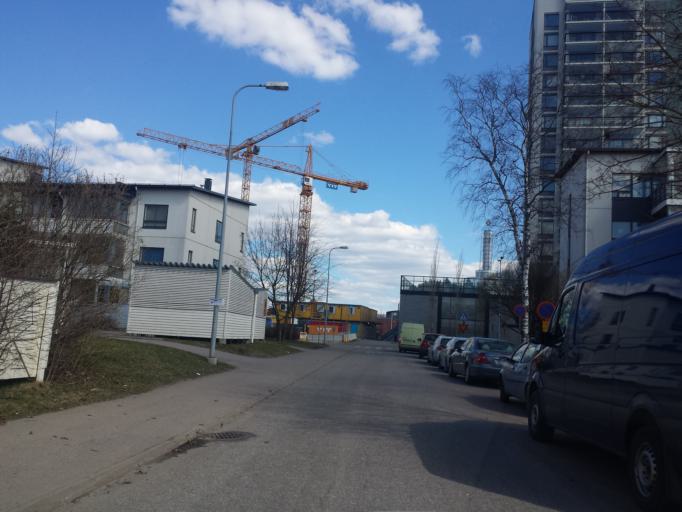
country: FI
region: Uusimaa
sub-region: Helsinki
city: Vantaa
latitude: 60.2874
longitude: 25.0294
